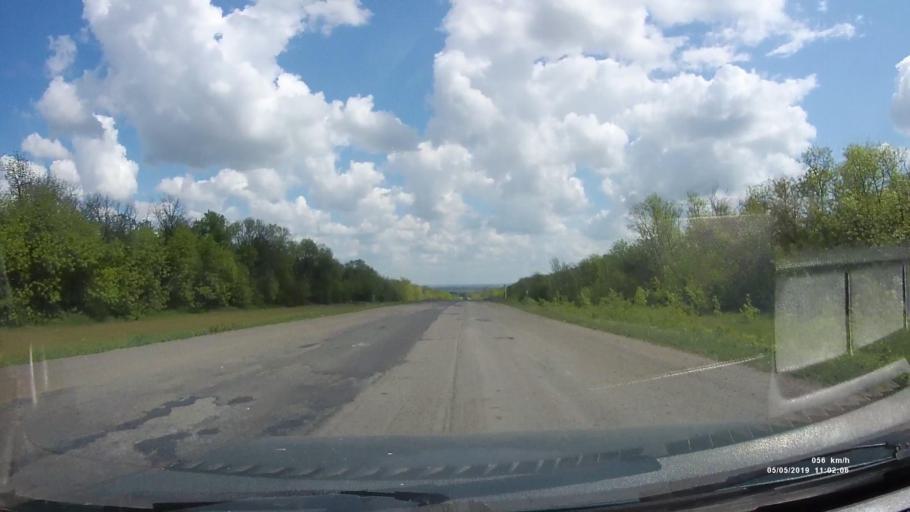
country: RU
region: Rostov
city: Ust'-Donetskiy
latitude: 47.6828
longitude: 40.9052
